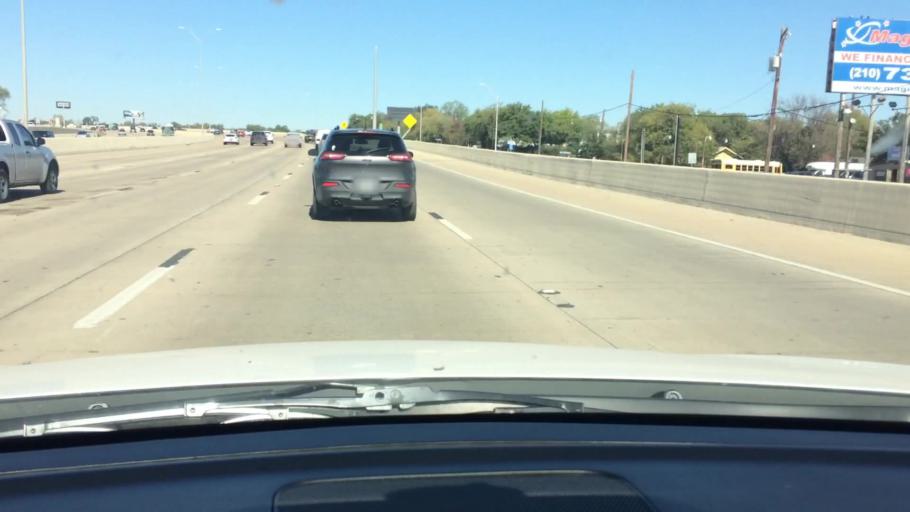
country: US
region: Texas
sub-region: Bexar County
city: Olmos Park
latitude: 29.4696
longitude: -98.5154
